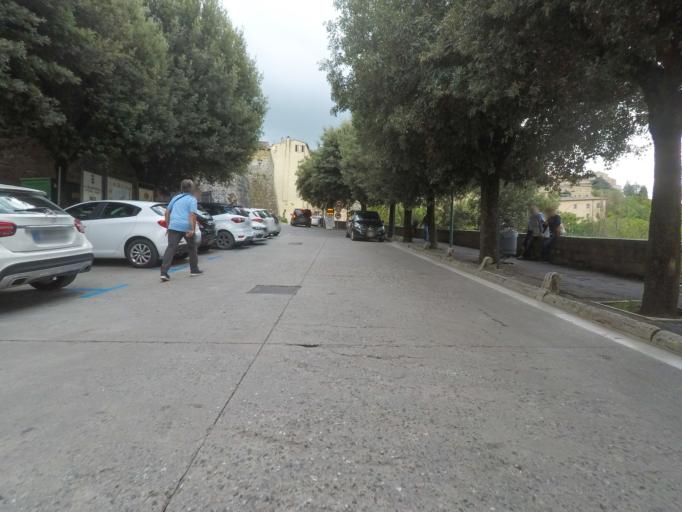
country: IT
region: Tuscany
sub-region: Provincia di Siena
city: Montepulciano
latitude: 43.0974
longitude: 11.7851
